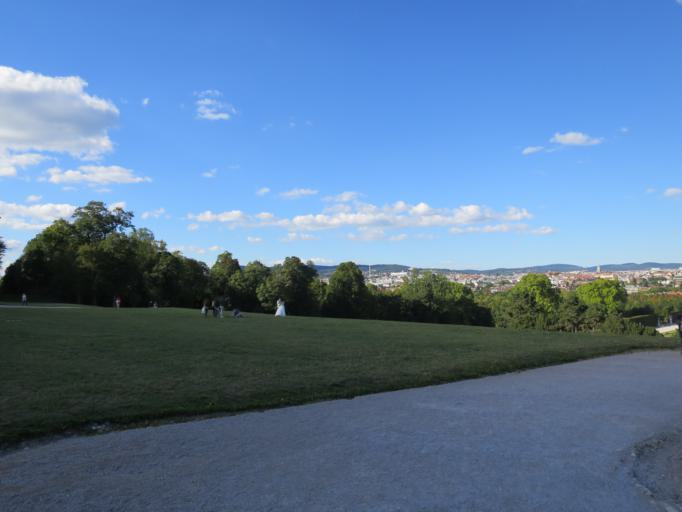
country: AT
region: Lower Austria
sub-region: Politischer Bezirk Modling
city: Vosendorf
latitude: 48.1800
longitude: 16.3102
